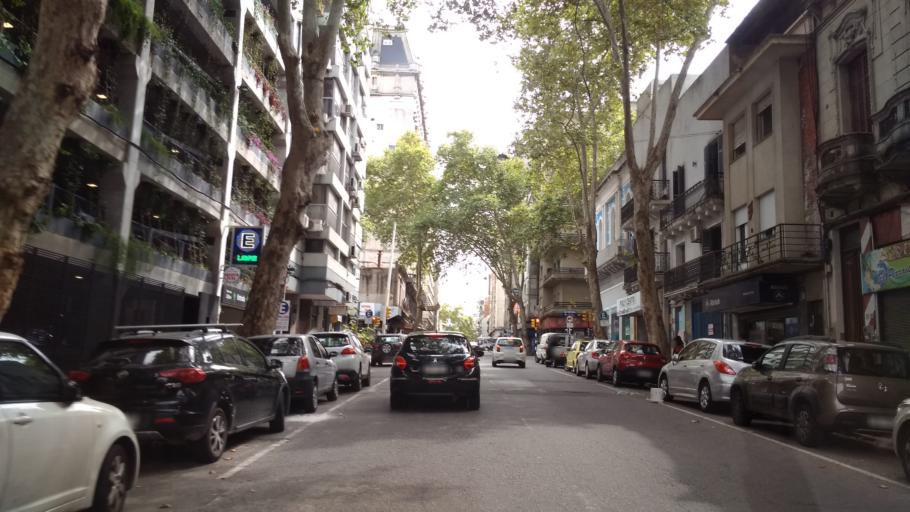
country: UY
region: Montevideo
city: Montevideo
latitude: -34.9079
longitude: -56.1980
